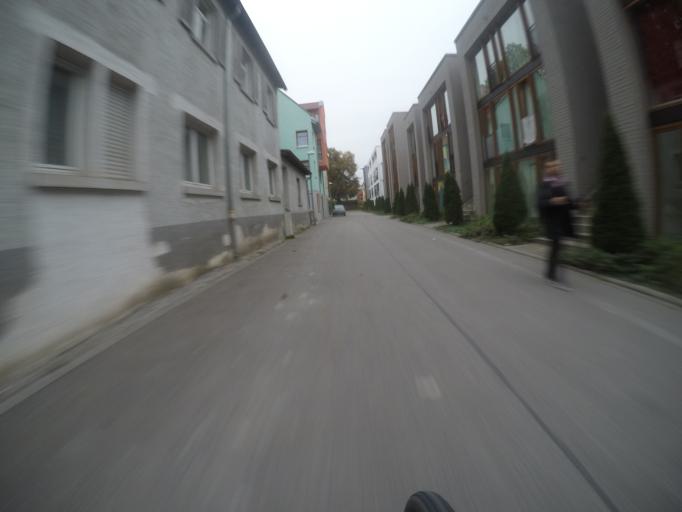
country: DE
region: Baden-Wuerttemberg
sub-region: Regierungsbezirk Stuttgart
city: Stuttgart-Ost
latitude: 48.7952
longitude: 9.2117
